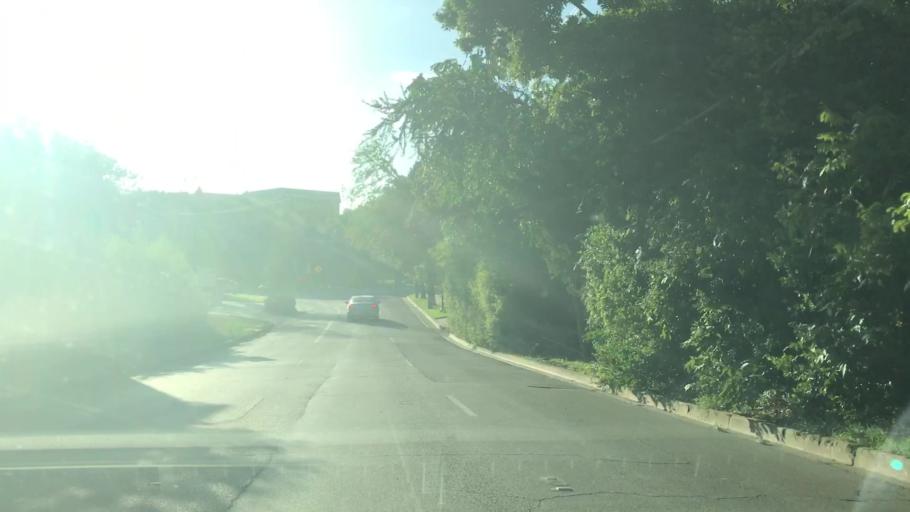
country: US
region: Texas
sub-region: Dallas County
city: Highland Park
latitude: 32.8192
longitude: -96.7985
